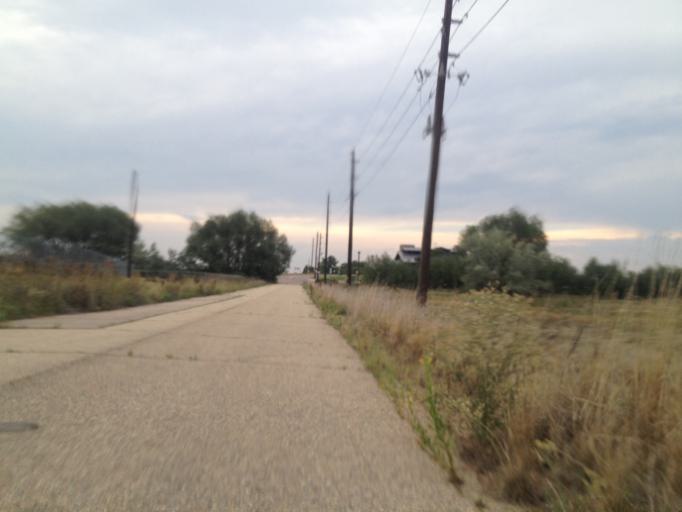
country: US
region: Colorado
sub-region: Boulder County
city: Louisville
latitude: 39.9484
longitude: -105.1281
